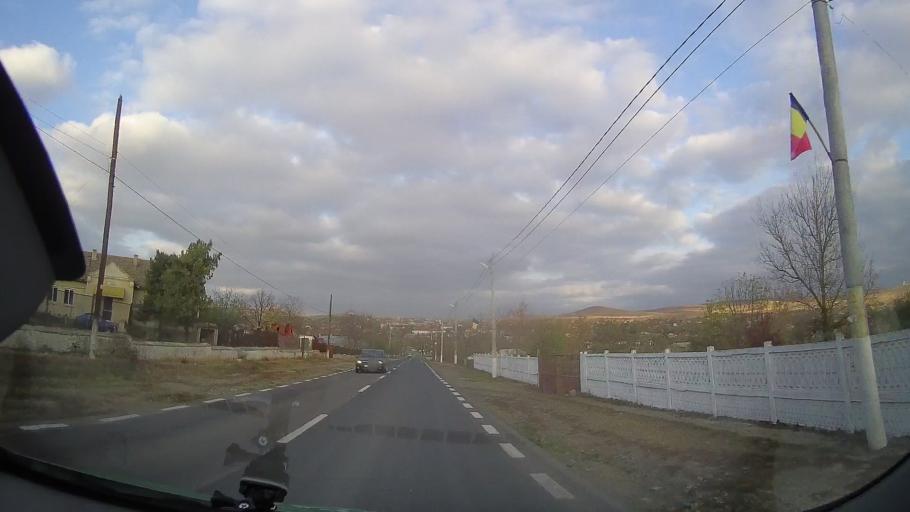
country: RO
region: Tulcea
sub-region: Comuna Topolog
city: Topolog
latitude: 44.8721
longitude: 28.3695
